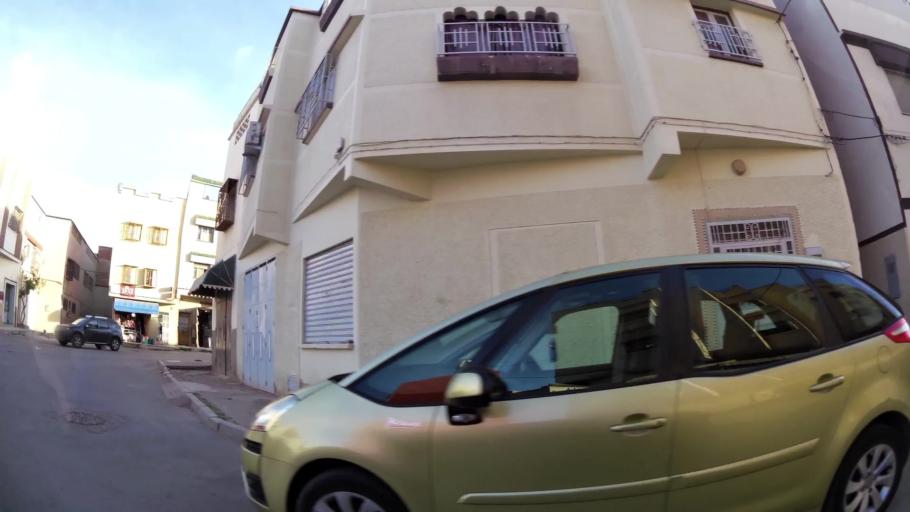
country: MA
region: Oriental
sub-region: Oujda-Angad
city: Oujda
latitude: 34.6755
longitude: -1.9011
